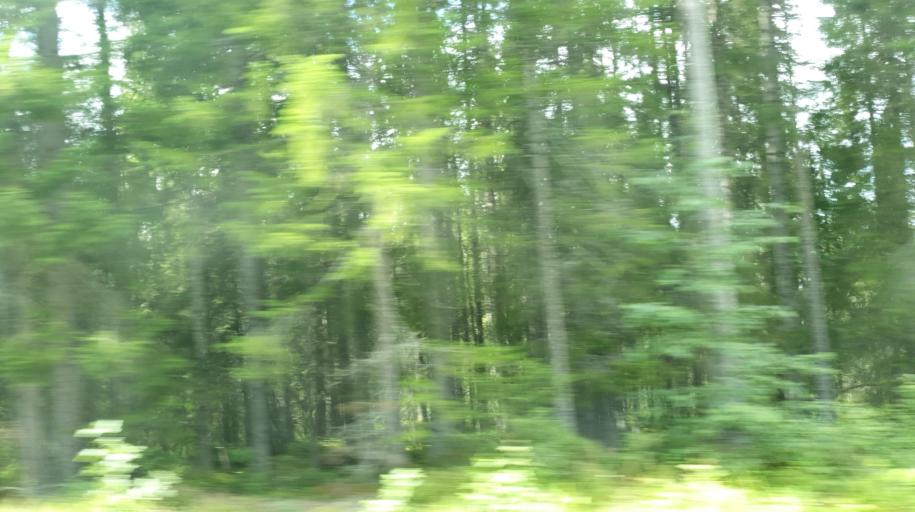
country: NO
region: Nord-Trondelag
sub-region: Levanger
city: Skogn
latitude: 63.6069
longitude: 11.2757
